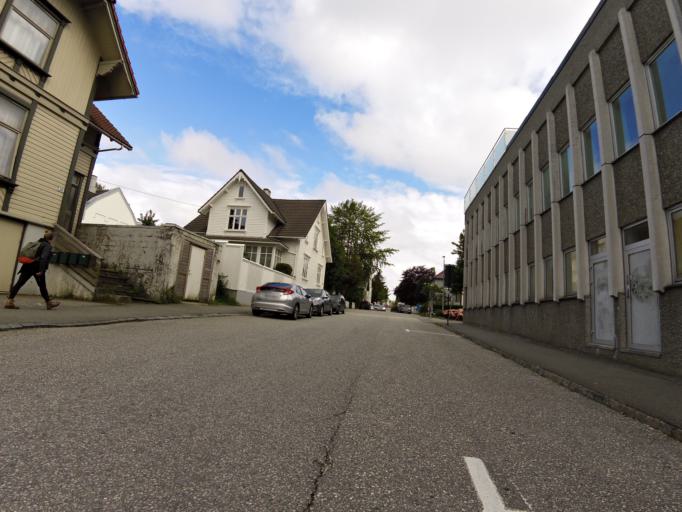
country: NO
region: Rogaland
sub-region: Stavanger
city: Stavanger
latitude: 58.9652
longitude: 5.7276
